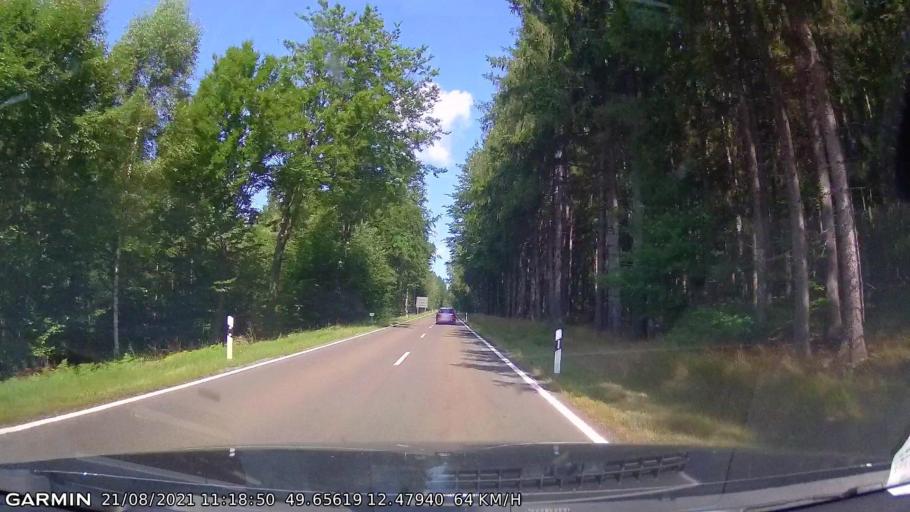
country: DE
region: Bavaria
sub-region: Upper Palatinate
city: Waidhaus
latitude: 49.6563
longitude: 12.4793
